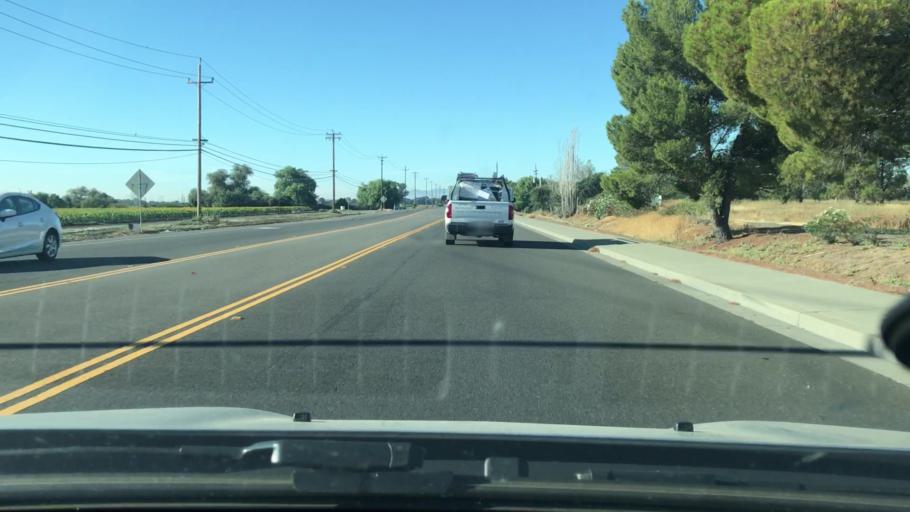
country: US
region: California
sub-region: Solano County
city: Hartley
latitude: 38.3715
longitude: -121.9340
